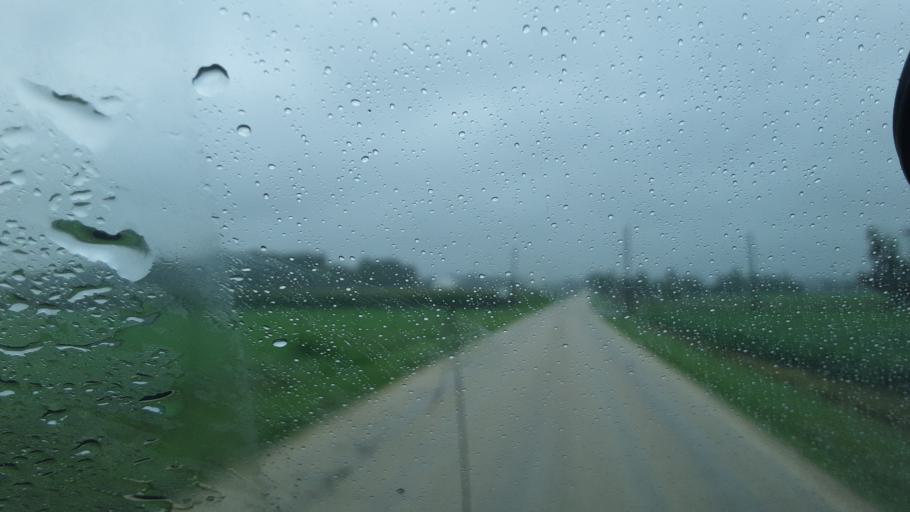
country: US
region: Indiana
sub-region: Adams County
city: Berne
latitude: 40.6877
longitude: -84.9086
